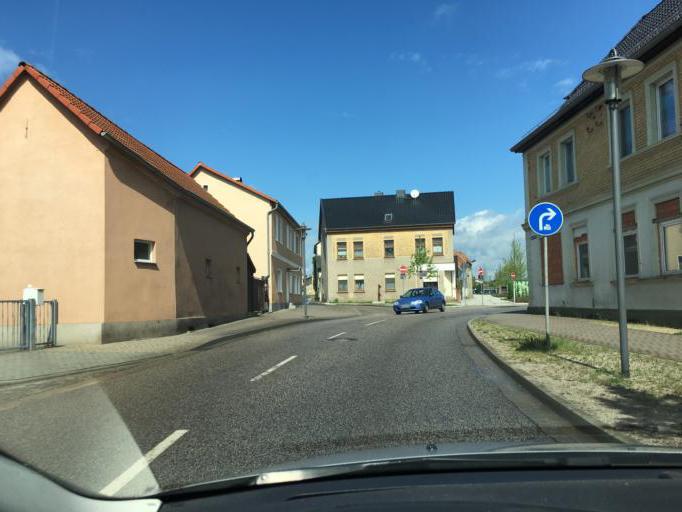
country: DE
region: Saxony-Anhalt
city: Haldensleben I
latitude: 52.2659
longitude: 11.4213
